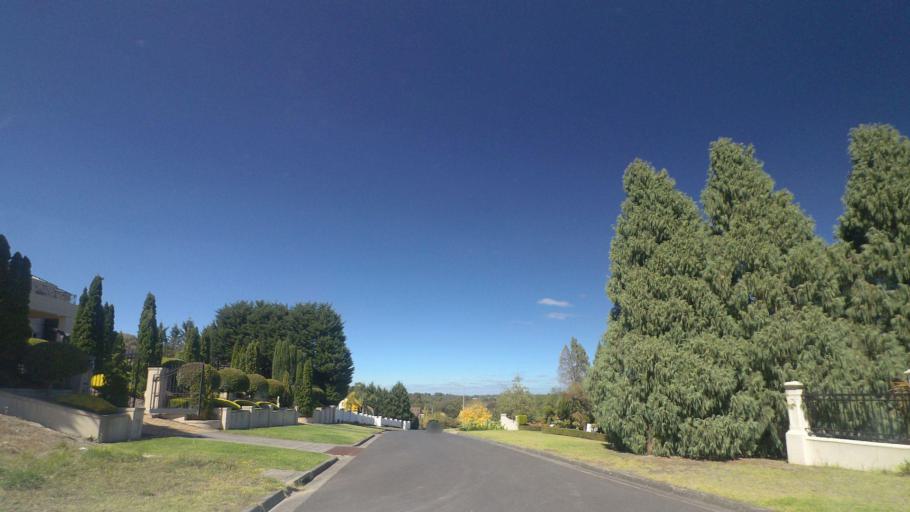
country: AU
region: Victoria
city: Mitcham
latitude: -37.8004
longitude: 145.2095
